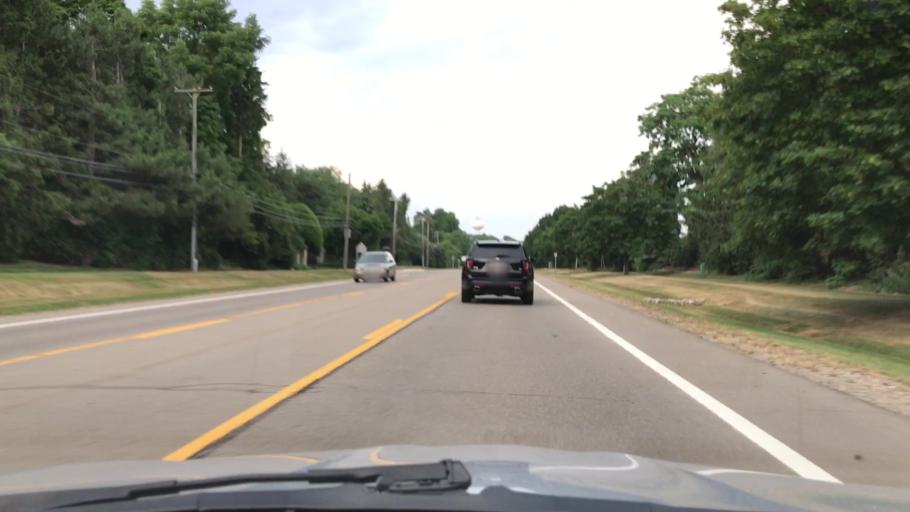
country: US
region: Michigan
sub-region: Wayne County
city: Northville
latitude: 42.4368
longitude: -83.5016
